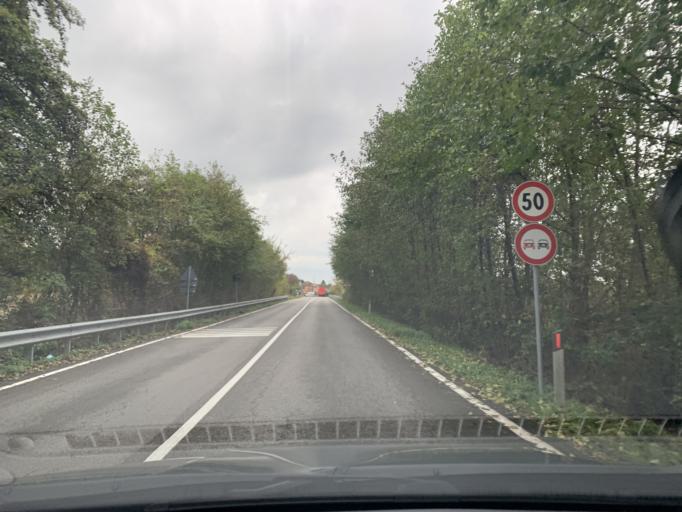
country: IT
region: Lombardy
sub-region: Provincia di Como
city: Casnate Con Bernate
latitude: 45.7655
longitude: 9.0653
